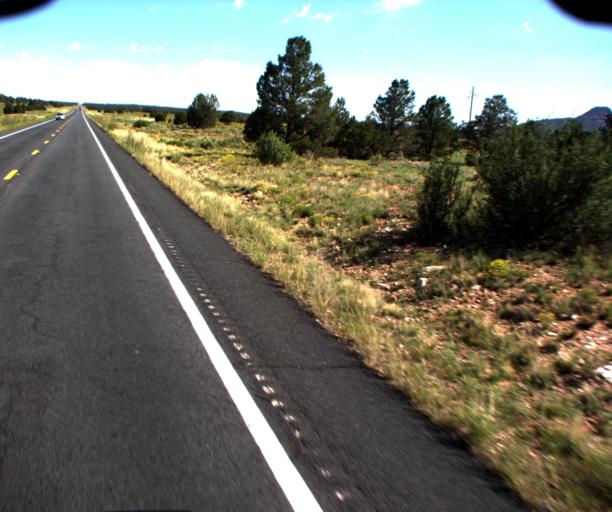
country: US
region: Arizona
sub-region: Coconino County
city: Grand Canyon Village
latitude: 35.7851
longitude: -112.1296
